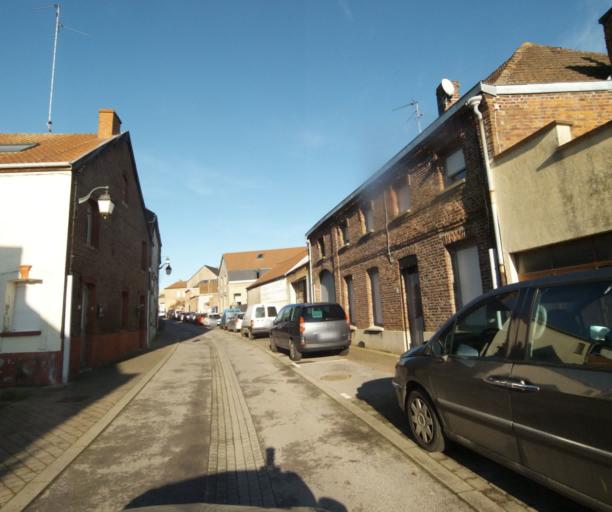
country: FR
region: Nord-Pas-de-Calais
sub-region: Departement du Nord
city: Aulnoy-lez-Valenciennes
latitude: 50.3316
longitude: 3.5287
